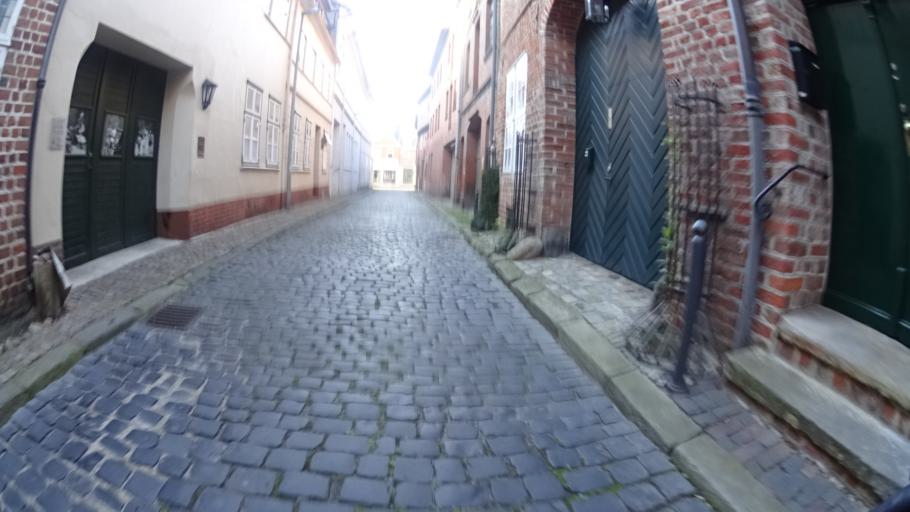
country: DE
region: Lower Saxony
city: Lueneburg
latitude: 53.2510
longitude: 10.4101
